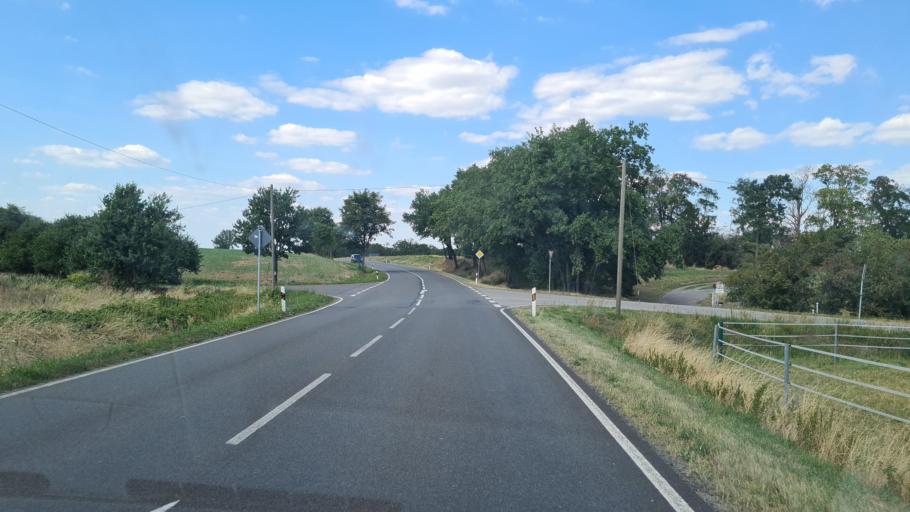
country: DE
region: Saxony
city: Machern
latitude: 51.4027
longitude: 12.6452
